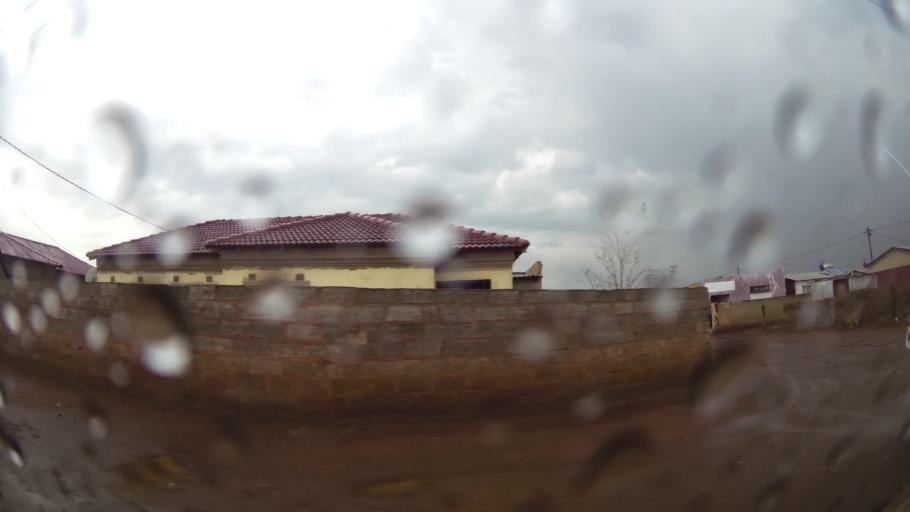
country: ZA
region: Gauteng
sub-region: Ekurhuleni Metropolitan Municipality
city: Germiston
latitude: -26.3739
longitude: 28.1510
